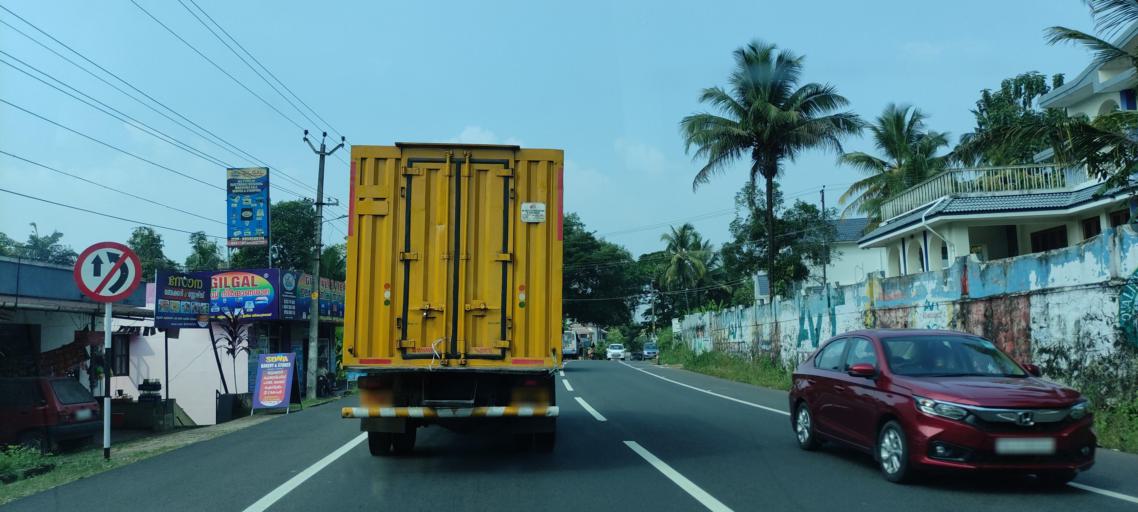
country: IN
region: Kerala
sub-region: Alappuzha
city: Chengannur
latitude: 9.2651
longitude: 76.6559
